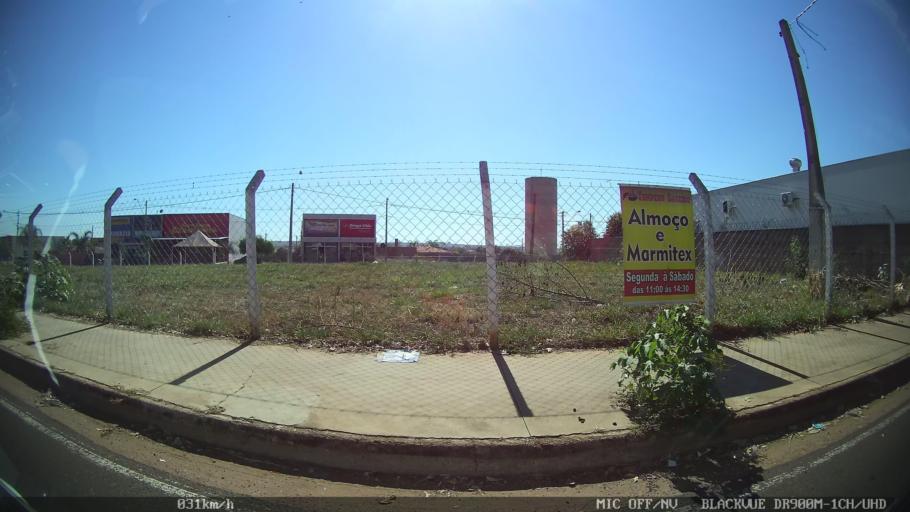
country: BR
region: Sao Paulo
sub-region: Sao Jose Do Rio Preto
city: Sao Jose do Rio Preto
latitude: -20.7671
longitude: -49.4204
